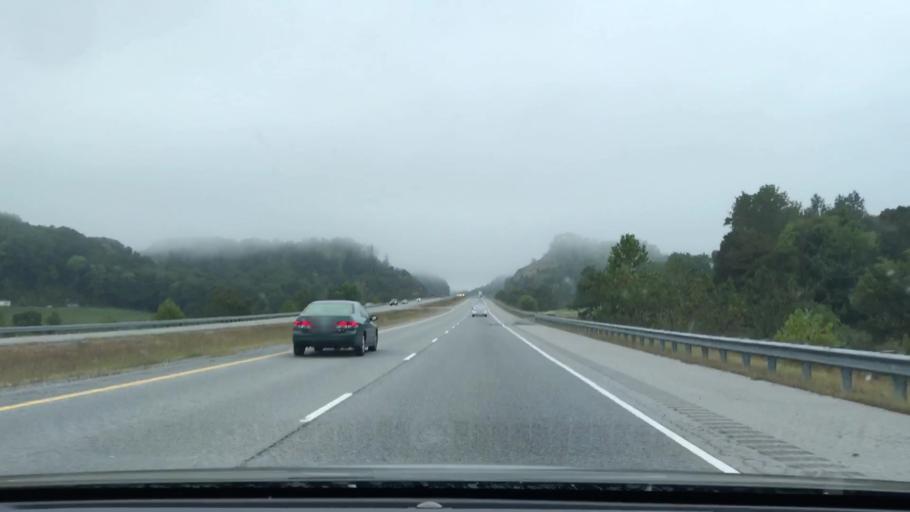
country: US
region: Tennessee
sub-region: Sumner County
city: Gallatin
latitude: 36.4565
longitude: -86.4668
